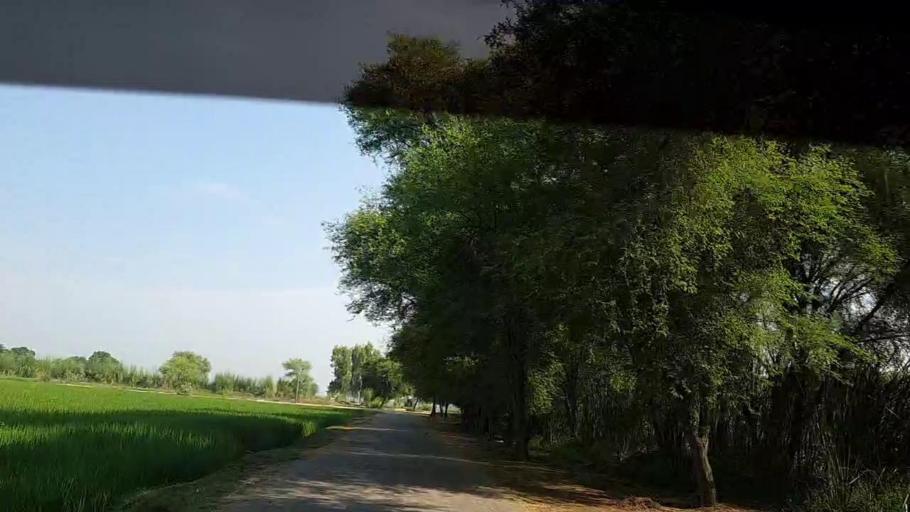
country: PK
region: Sindh
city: Shikarpur
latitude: 28.0921
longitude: 68.6773
